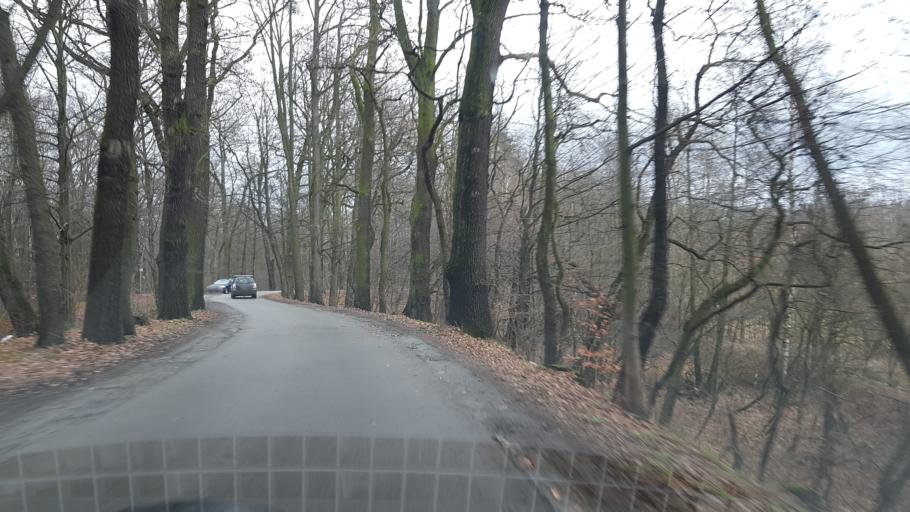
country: PL
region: Silesian Voivodeship
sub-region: Powiat pszczynski
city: Radostowice
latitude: 49.9748
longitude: 18.9035
